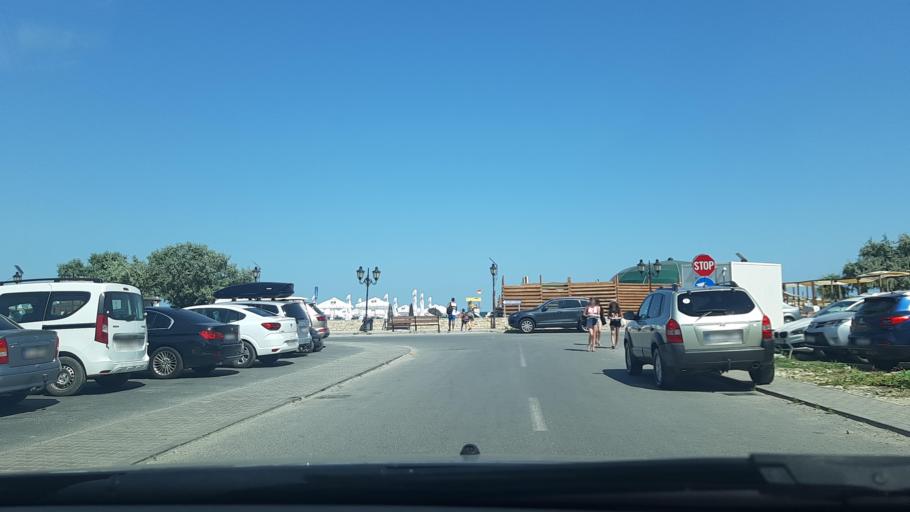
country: RO
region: Constanta
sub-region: Comuna Navodari
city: Navodari
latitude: 44.2997
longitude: 28.6254
